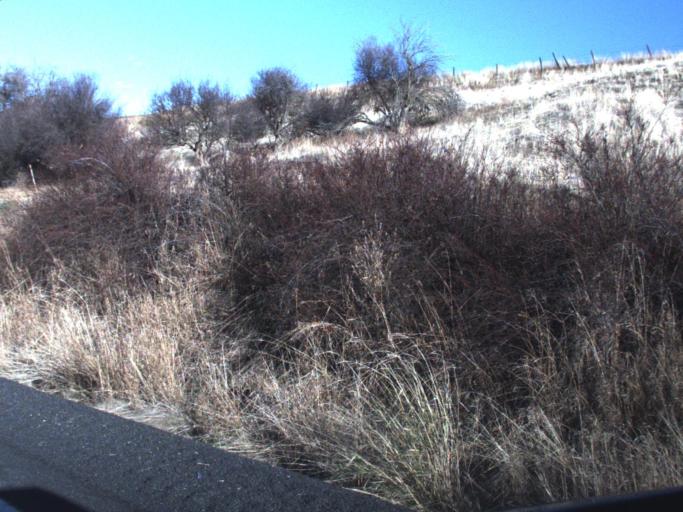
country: US
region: Washington
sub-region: Whitman County
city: Pullman
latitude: 46.7234
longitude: -117.2869
